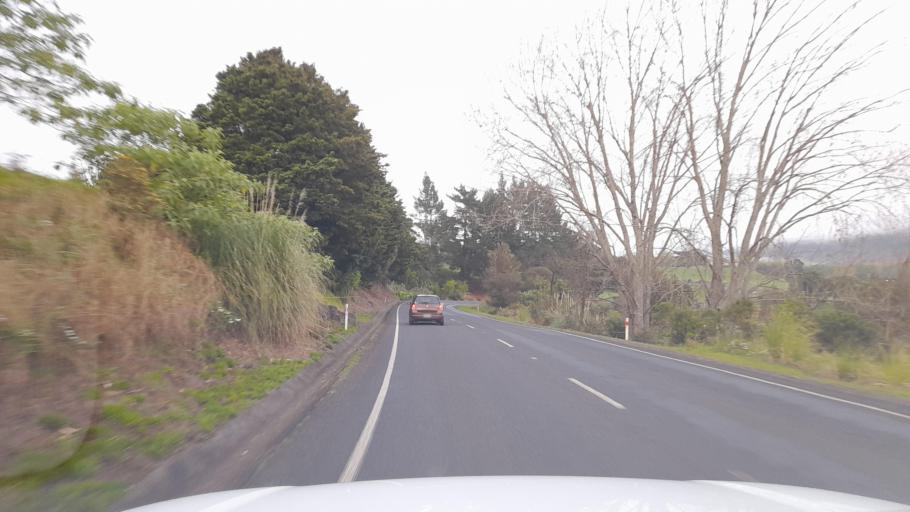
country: NZ
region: Northland
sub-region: Whangarei
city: Maungatapere
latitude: -35.7088
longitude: 173.9893
